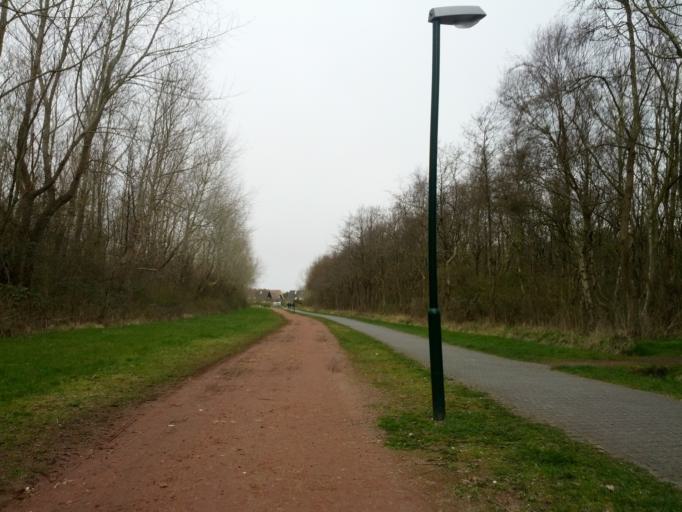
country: DE
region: Lower Saxony
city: Langeoog
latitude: 53.7393
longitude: 7.4807
